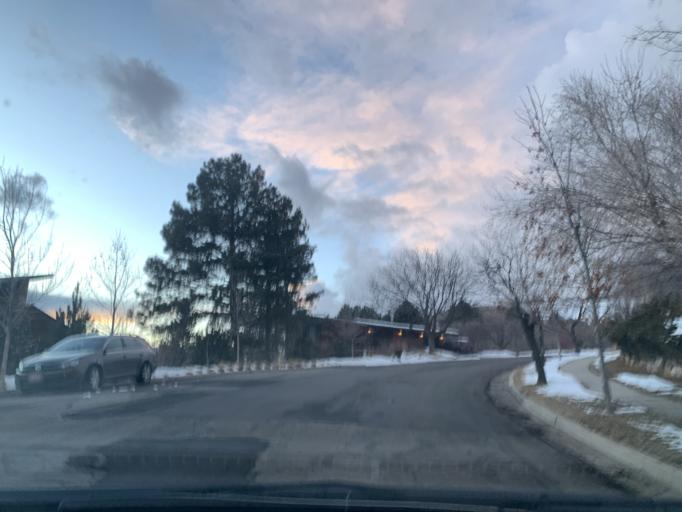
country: US
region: Utah
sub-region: Salt Lake County
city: Salt Lake City
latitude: 40.7816
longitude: -111.8446
